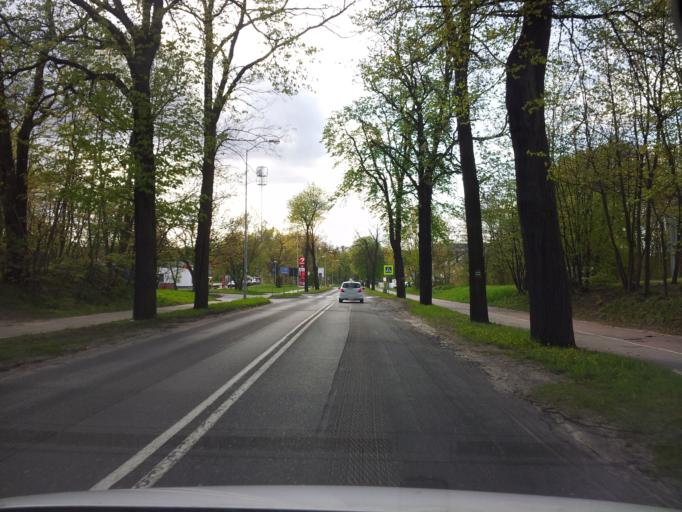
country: PL
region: Lubusz
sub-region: Zielona Gora
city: Zielona Gora
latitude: 51.9393
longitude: 15.4710
